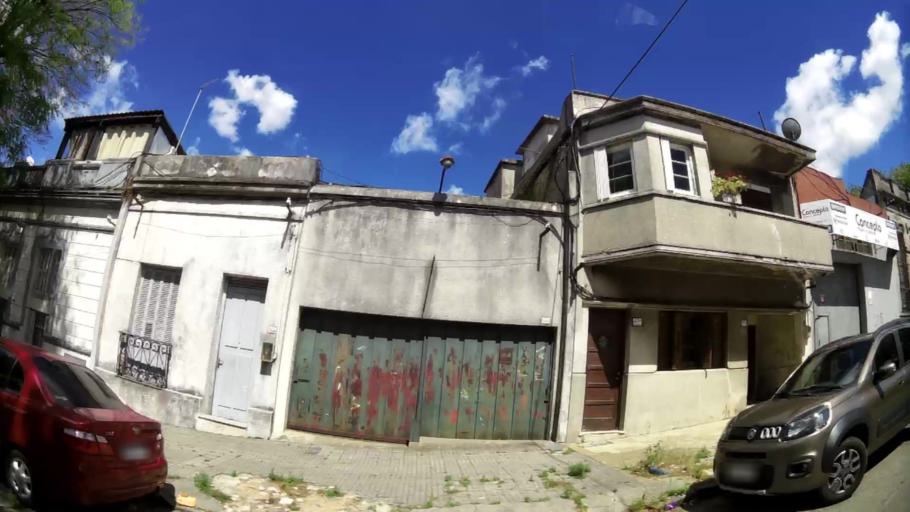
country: UY
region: Montevideo
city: Montevideo
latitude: -34.8793
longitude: -56.1926
